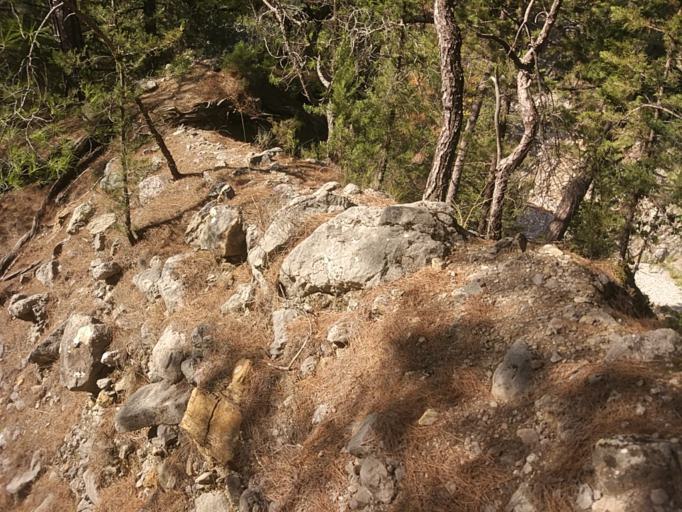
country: TR
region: Antalya
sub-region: Kemer
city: Goeynuek
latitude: 36.6792
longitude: 30.4904
